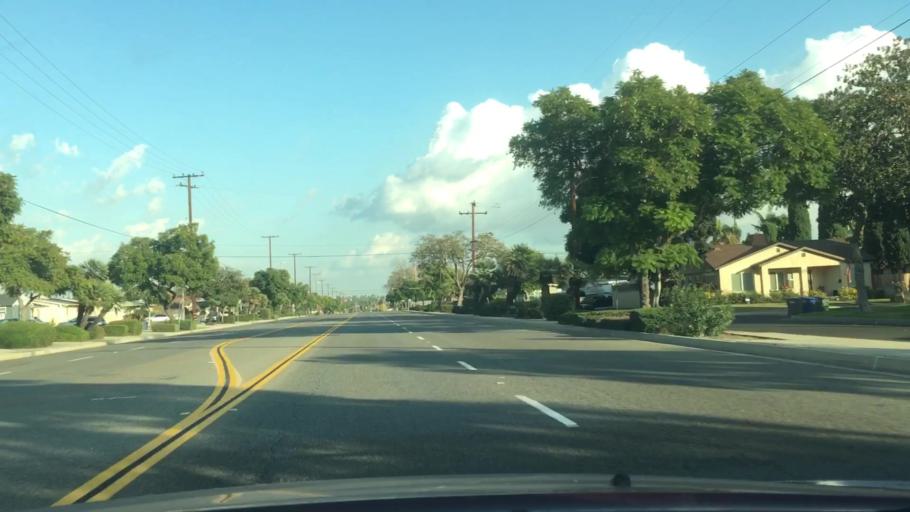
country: US
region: California
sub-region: Orange County
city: Buena Park
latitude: 33.8881
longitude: -118.0083
